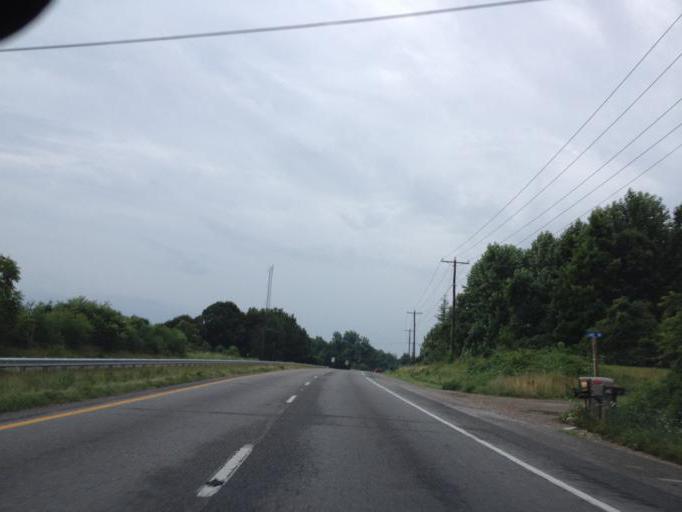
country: US
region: Maryland
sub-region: Queen Anne's County
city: Centreville
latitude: 38.9489
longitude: -76.0661
